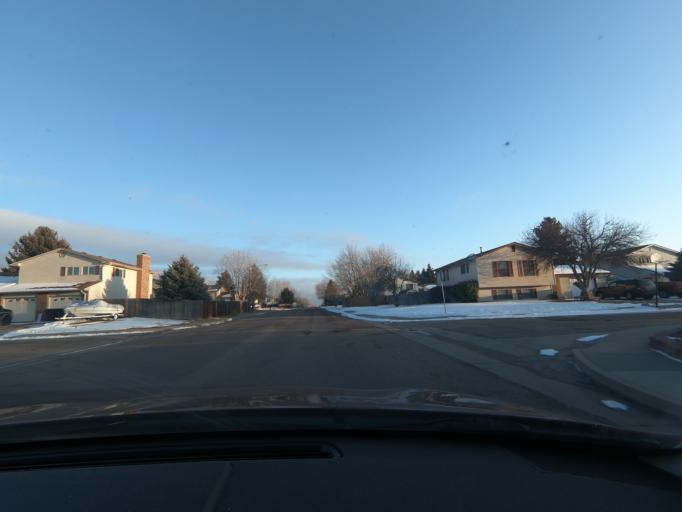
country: US
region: Colorado
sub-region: El Paso County
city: Security-Widefield
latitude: 38.7342
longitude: -104.6885
